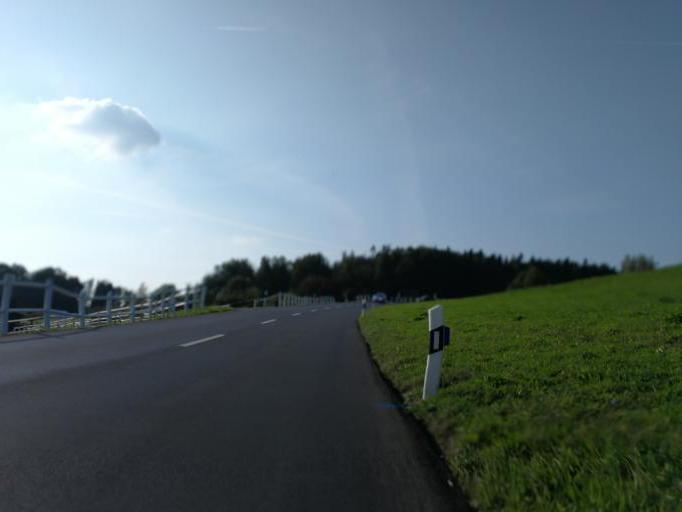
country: CH
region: Zurich
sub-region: Bezirk Meilen
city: Stafa
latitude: 47.2551
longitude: 8.7198
